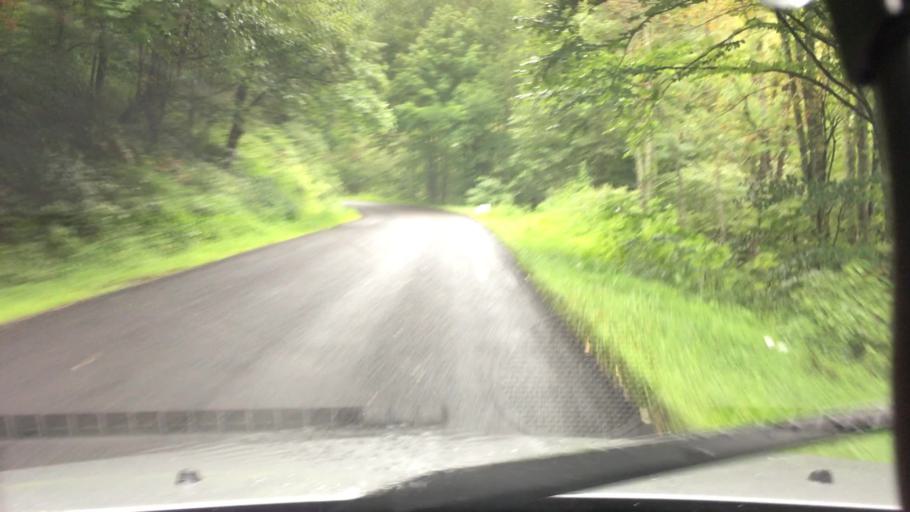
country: US
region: North Carolina
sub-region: Madison County
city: Mars Hill
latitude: 35.9118
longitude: -82.5365
